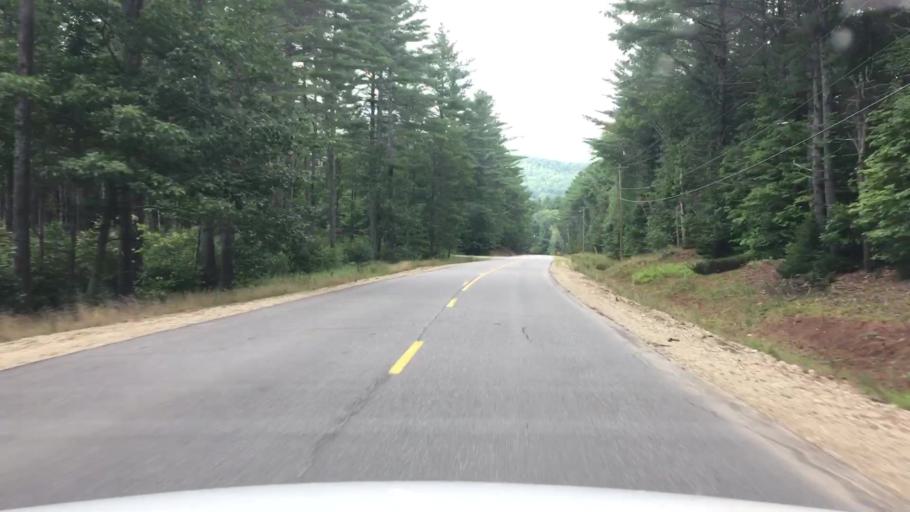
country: US
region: Maine
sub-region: Oxford County
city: Rumford
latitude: 44.5442
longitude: -70.6781
